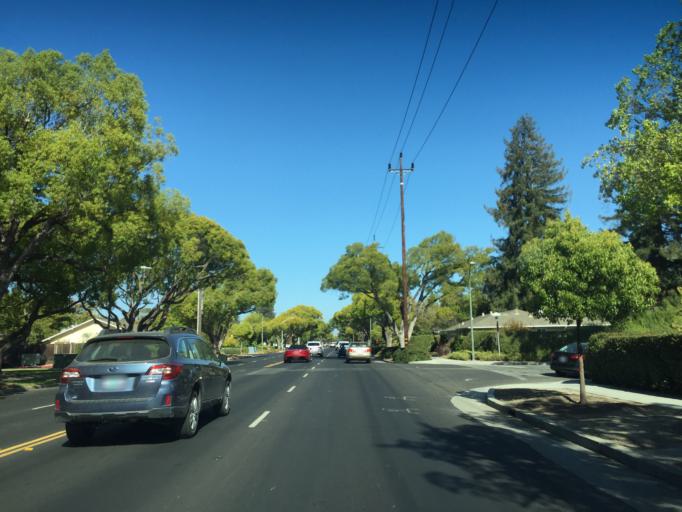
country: US
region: California
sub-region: Santa Clara County
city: Palo Alto
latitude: 37.4436
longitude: -122.1380
